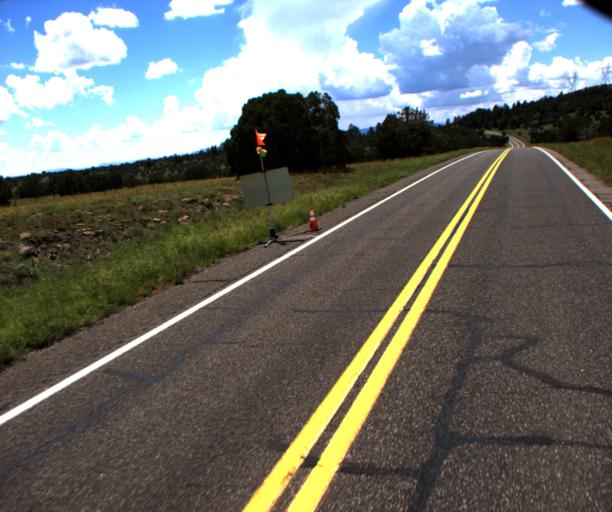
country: US
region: Arizona
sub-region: Gila County
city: Pine
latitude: 34.5157
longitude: -111.5332
